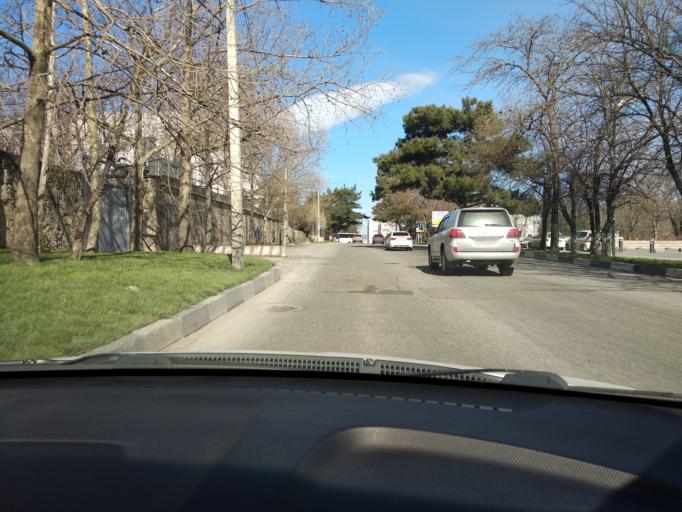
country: RU
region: Krasnodarskiy
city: Novorossiysk
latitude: 44.7171
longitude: 37.7721
